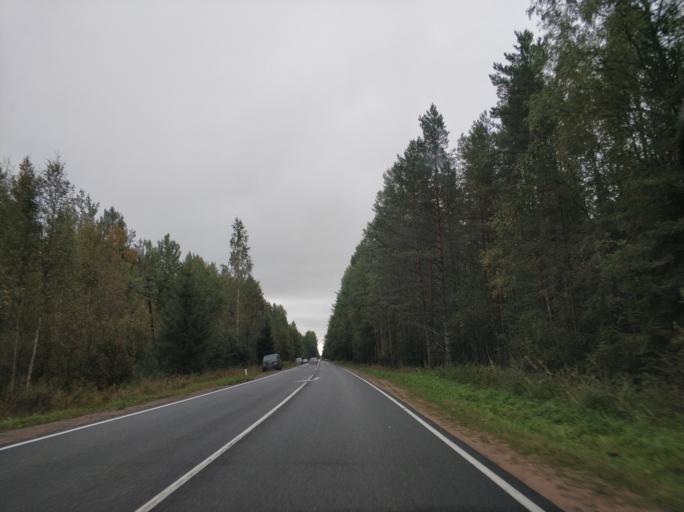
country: RU
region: Leningrad
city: Borisova Griva
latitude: 60.1600
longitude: 30.9240
